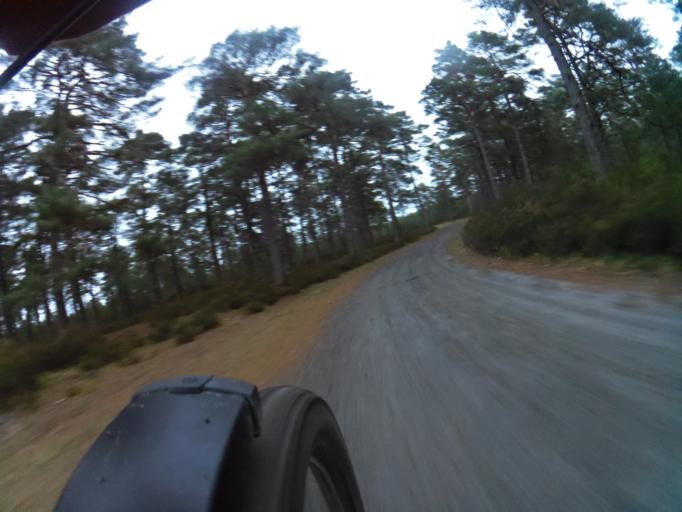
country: PL
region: Pomeranian Voivodeship
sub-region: Powiat wejherowski
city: Choczewo
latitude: 54.7995
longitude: 17.7806
